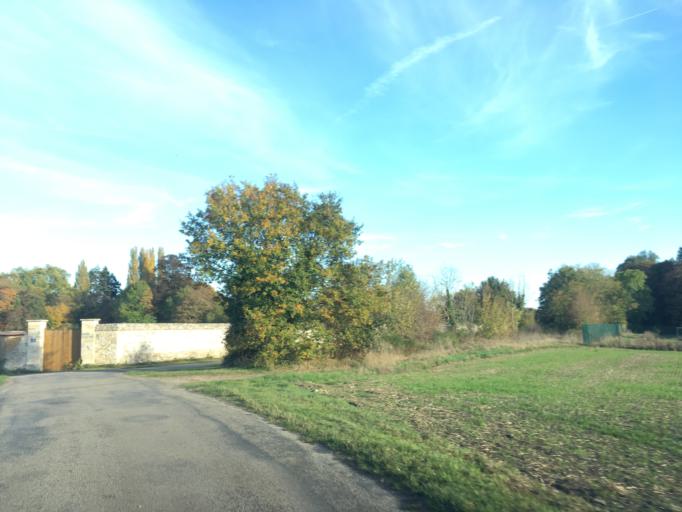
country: FR
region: Haute-Normandie
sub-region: Departement de l'Eure
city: Heudreville-sur-Eure
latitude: 49.1094
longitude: 1.2311
